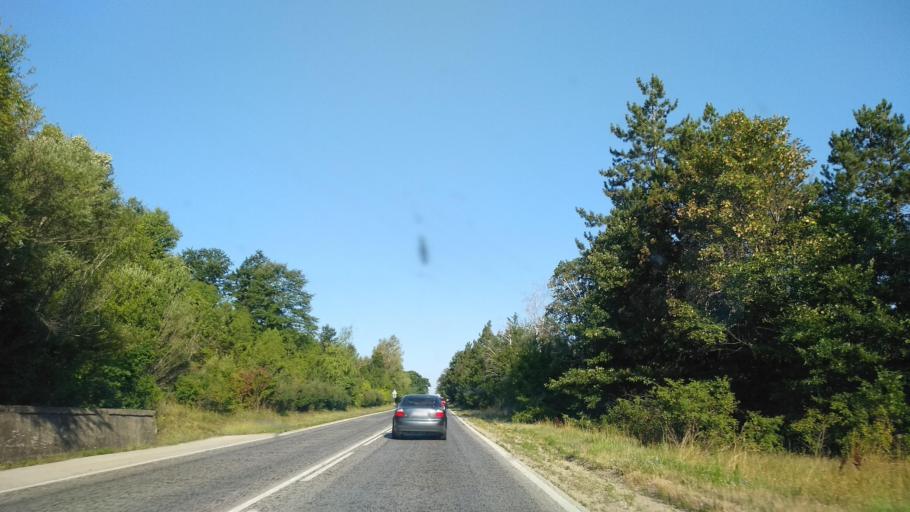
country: BG
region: Gabrovo
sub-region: Obshtina Sevlievo
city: Sevlievo
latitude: 43.0478
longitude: 24.9305
